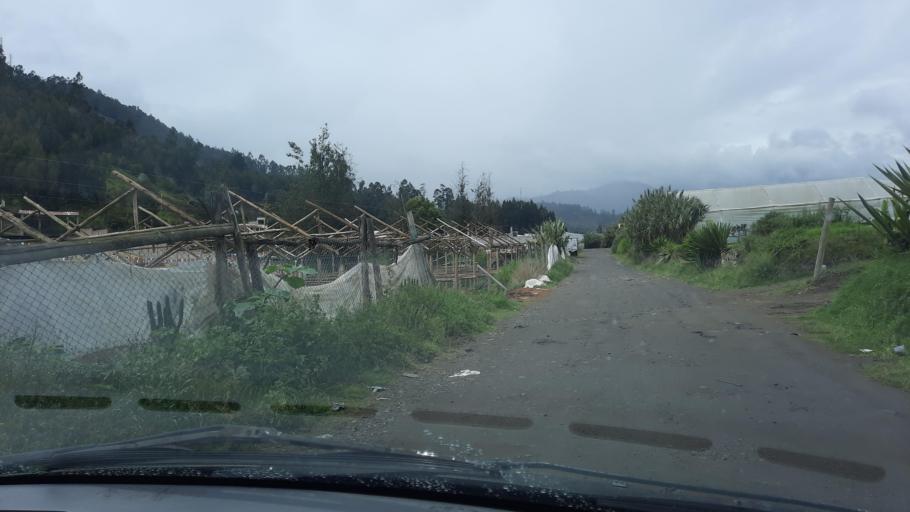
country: EC
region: Chimborazo
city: Riobamba
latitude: -1.6898
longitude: -78.6611
